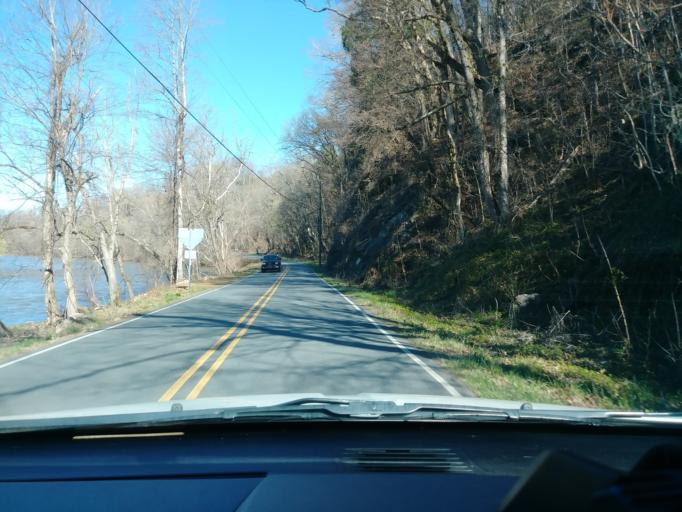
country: US
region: North Carolina
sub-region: Madison County
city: Marshall
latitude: 35.8952
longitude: -82.8228
